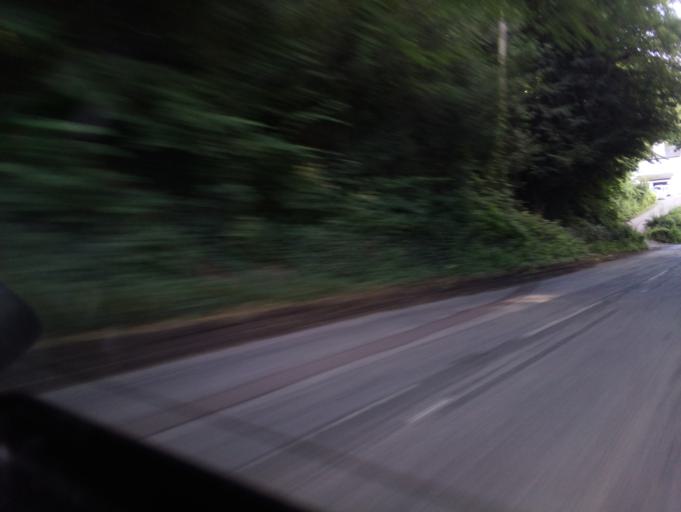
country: GB
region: England
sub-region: Herefordshire
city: Walford
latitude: 51.8724
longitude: -2.6048
